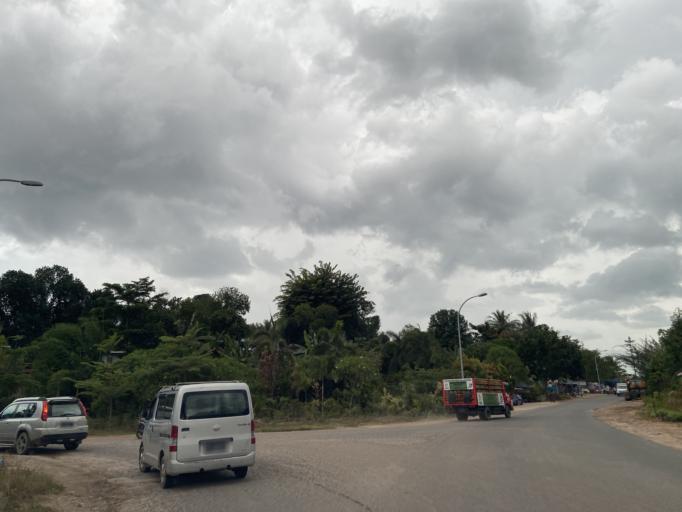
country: SG
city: Singapore
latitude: 1.1071
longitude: 104.0480
